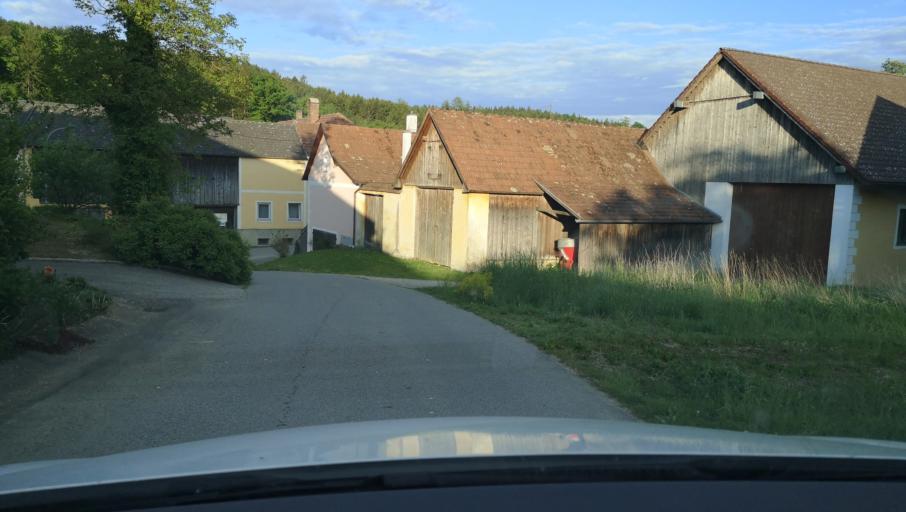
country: AT
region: Lower Austria
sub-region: Politischer Bezirk Melk
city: Blindenmarkt
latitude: 48.1413
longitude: 14.9900
